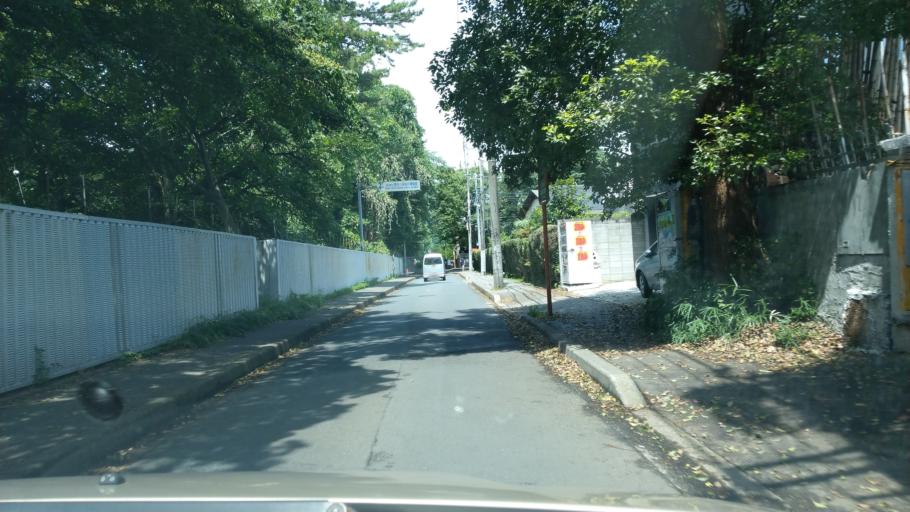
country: JP
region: Saitama
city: Saitama
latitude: 35.9203
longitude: 139.6336
